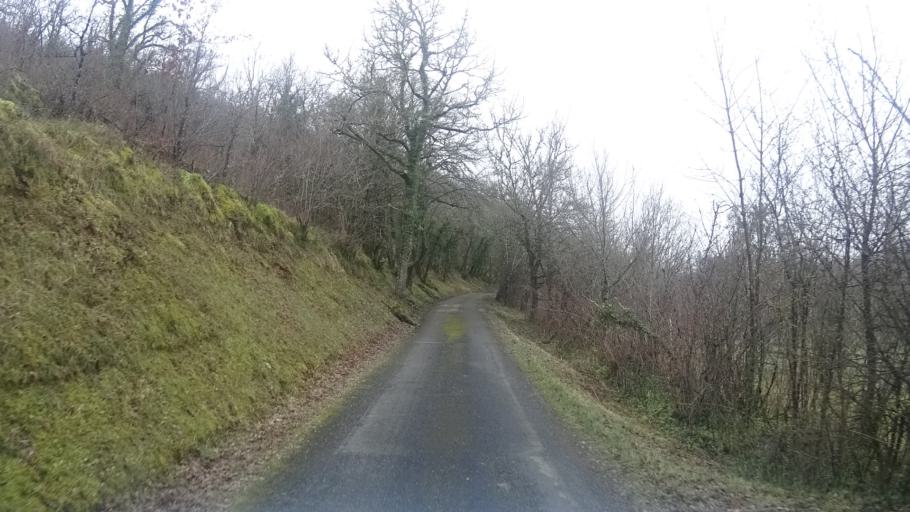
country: FR
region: Aquitaine
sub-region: Departement de la Dordogne
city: Terrasson-Lavilledieu
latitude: 45.1118
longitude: 1.2369
